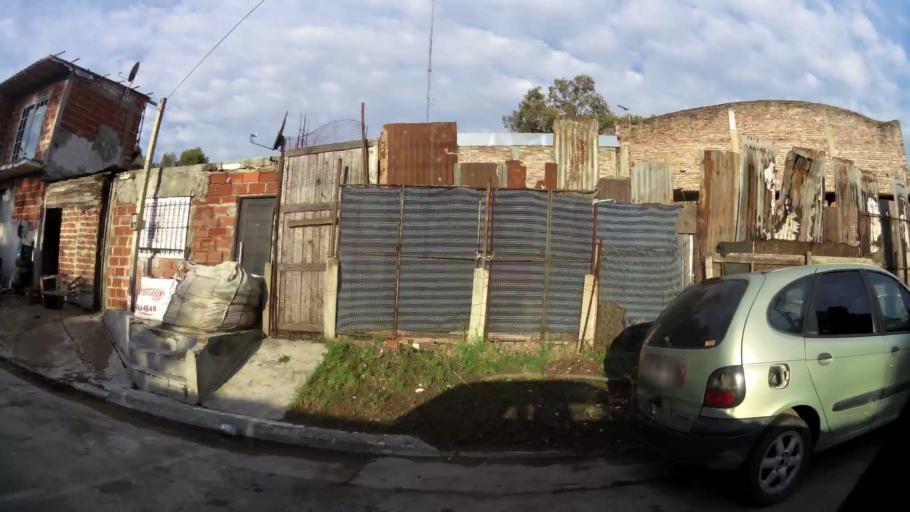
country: AR
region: Buenos Aires
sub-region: Partido de Lomas de Zamora
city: Lomas de Zamora
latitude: -34.7597
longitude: -58.3642
